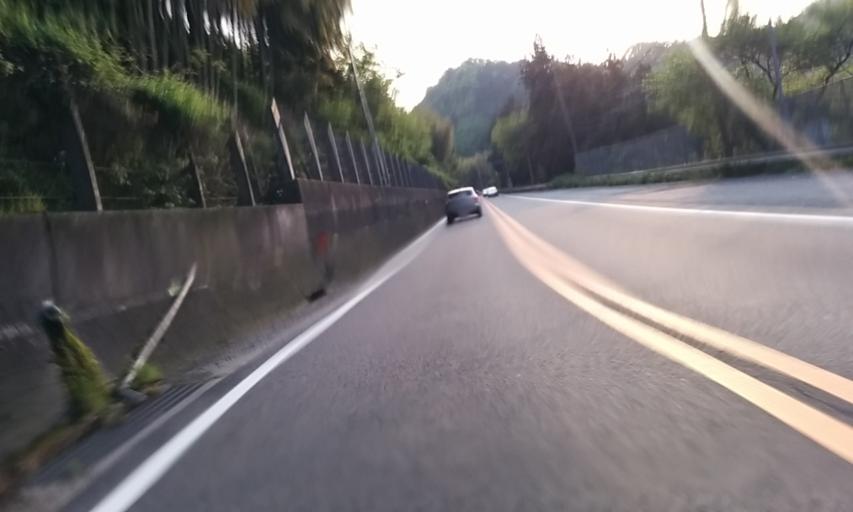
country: JP
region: Ehime
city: Saijo
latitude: 33.8244
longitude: 132.9856
